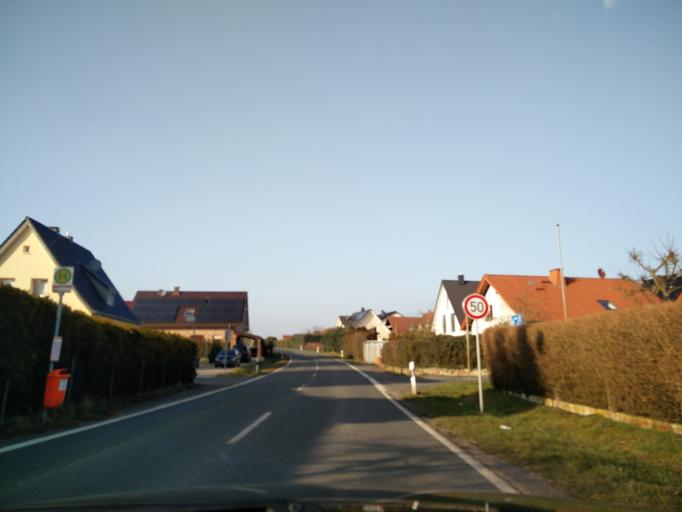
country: DE
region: North Rhine-Westphalia
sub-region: Regierungsbezirk Detmold
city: Paderborn
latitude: 51.6803
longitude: 8.6965
